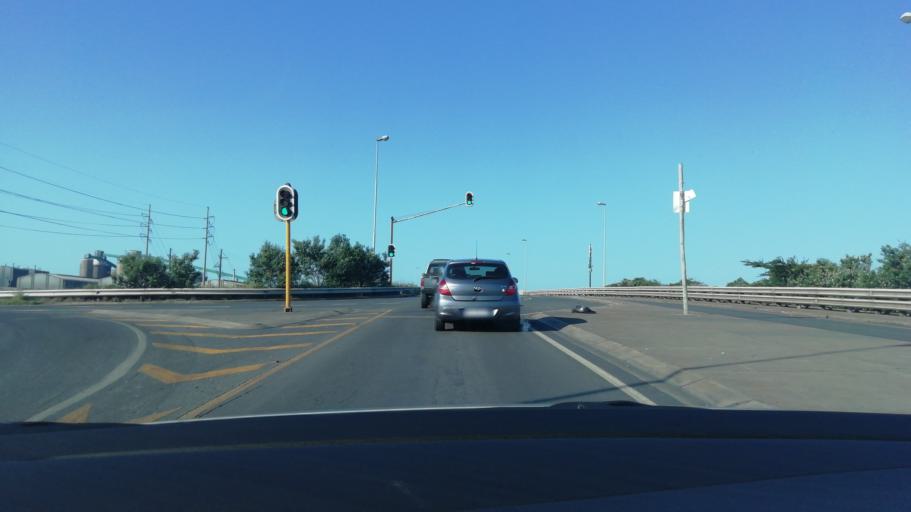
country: ZA
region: KwaZulu-Natal
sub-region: uThungulu District Municipality
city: Richards Bay
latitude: -28.7718
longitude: 32.0335
